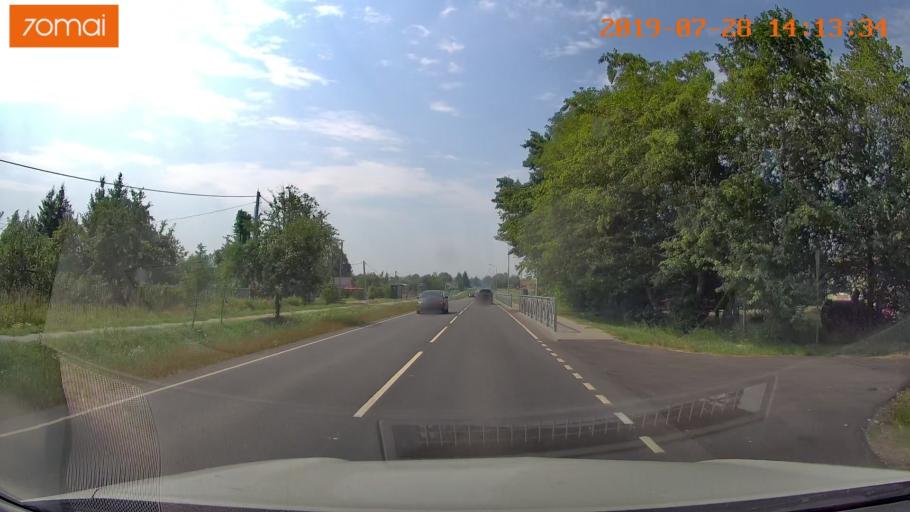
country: RU
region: Kaliningrad
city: Vzmorye
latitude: 54.8199
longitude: 20.3006
